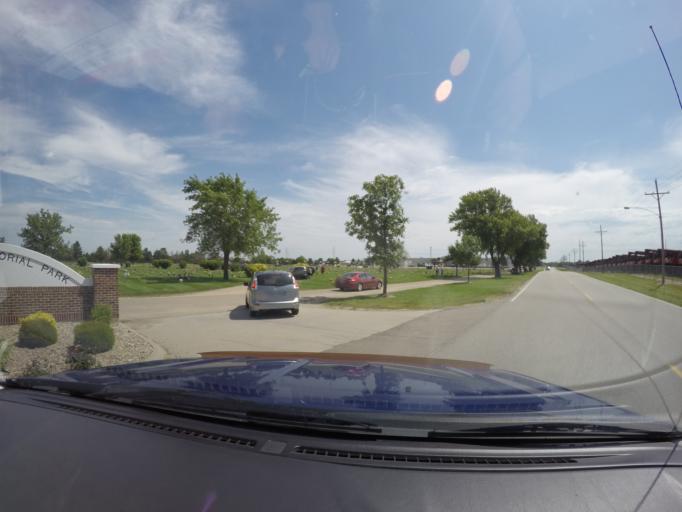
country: US
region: Nebraska
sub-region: Hall County
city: Grand Island
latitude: 40.9025
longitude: -98.3907
